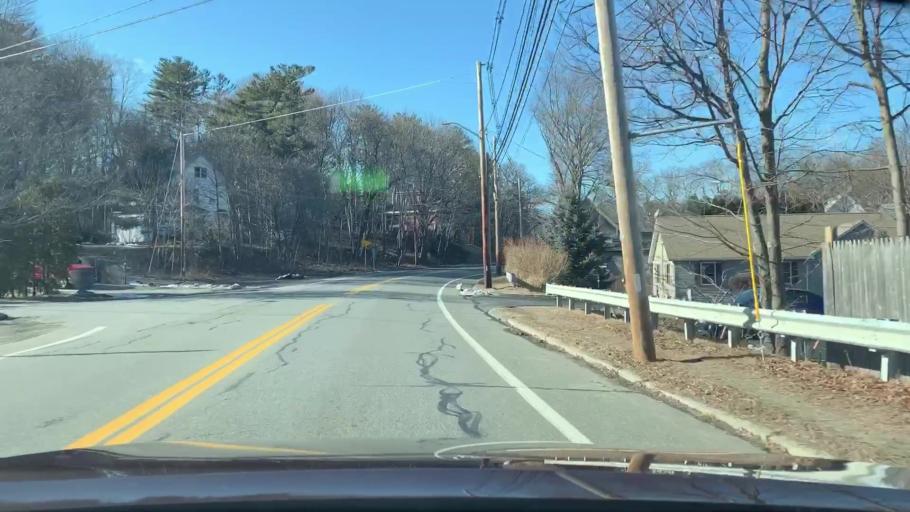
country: US
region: Massachusetts
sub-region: Essex County
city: Gloucester
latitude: 42.6143
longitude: -70.6939
